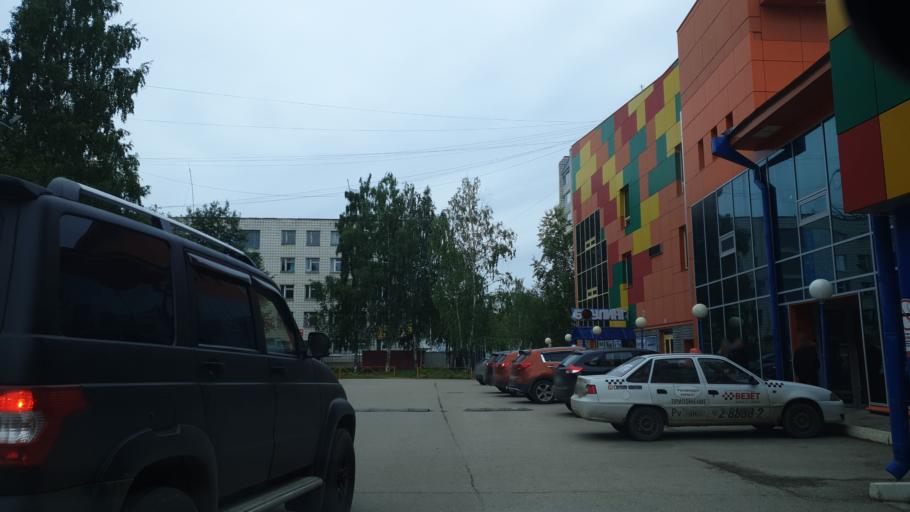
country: RU
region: Komi Republic
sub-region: Syktyvdinskiy Rayon
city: Syktyvkar
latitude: 61.6623
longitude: 50.8307
